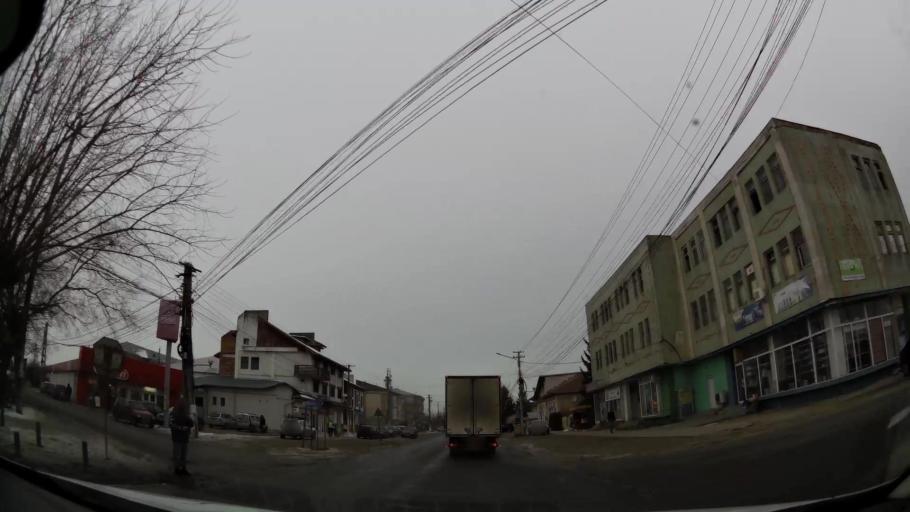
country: RO
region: Dambovita
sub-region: Comuna Racari
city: Racari
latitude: 44.6257
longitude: 25.7431
